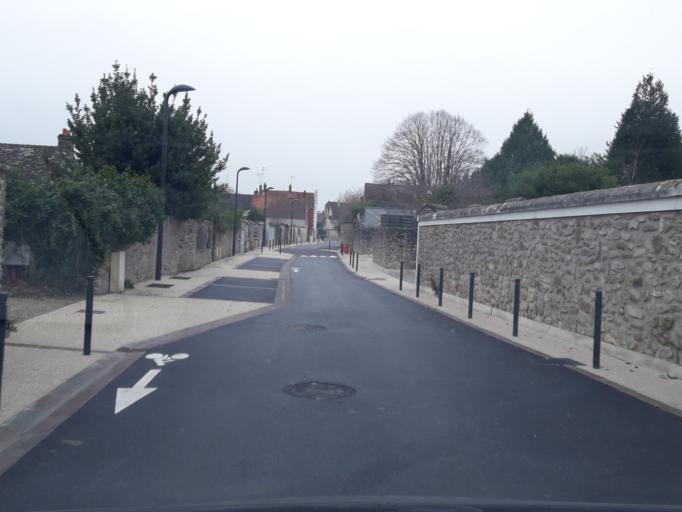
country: FR
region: Ile-de-France
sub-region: Departement de l'Essonne
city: Vert-le-Petit
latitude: 48.5550
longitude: 2.3712
